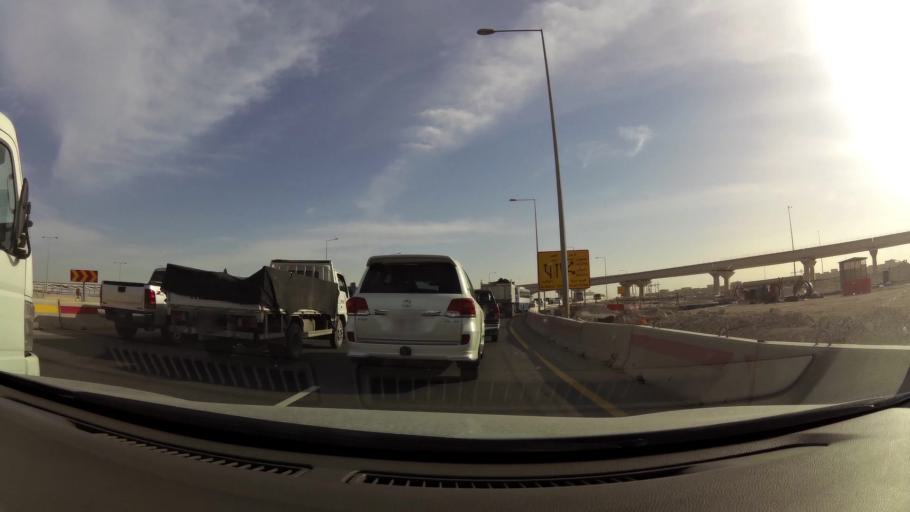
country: QA
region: Al Wakrah
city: Al Wakrah
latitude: 25.2165
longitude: 51.5854
